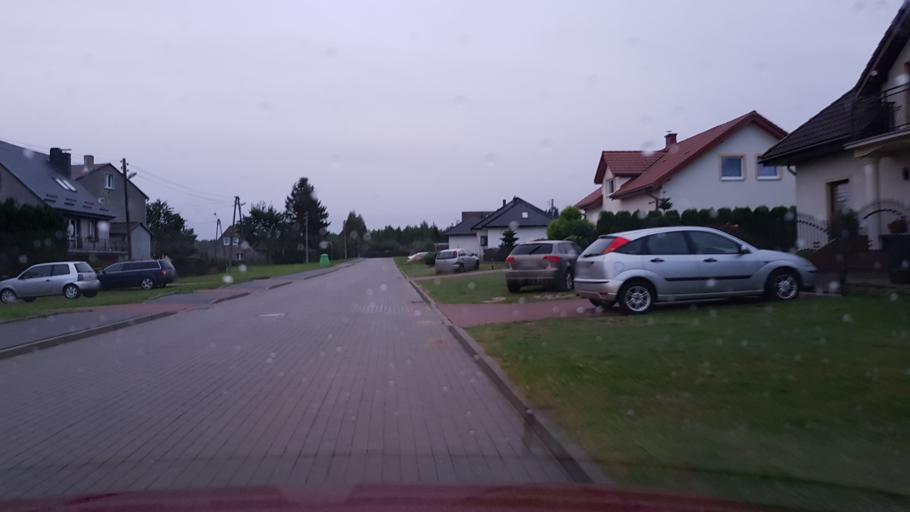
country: PL
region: West Pomeranian Voivodeship
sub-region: Powiat slawienski
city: Slawno
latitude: 54.3443
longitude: 16.6739
